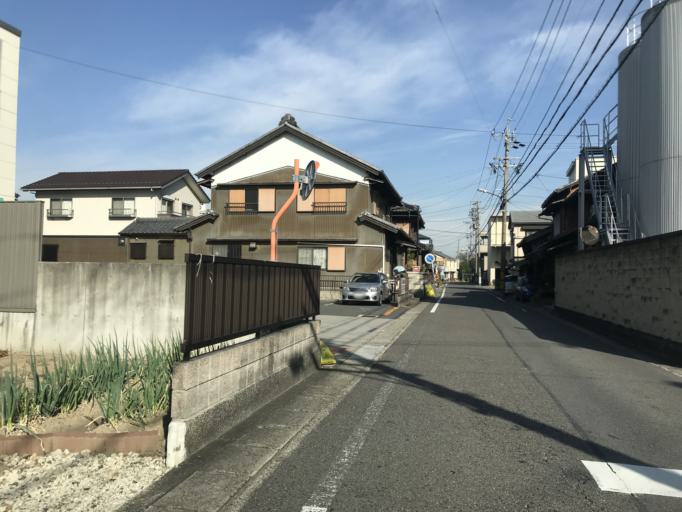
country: JP
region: Aichi
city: Inazawa
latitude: 35.2123
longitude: 136.8400
